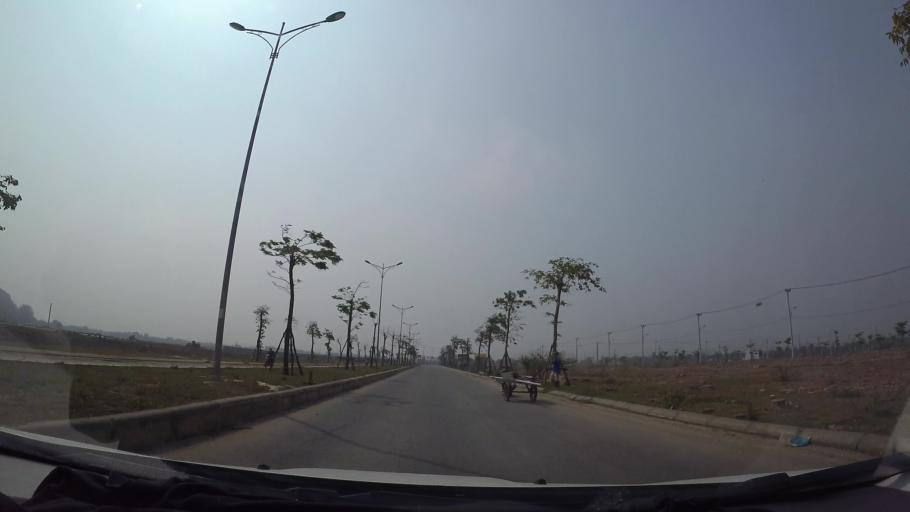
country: VN
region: Da Nang
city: Ngu Hanh Son
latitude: 16.0011
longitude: 108.2471
